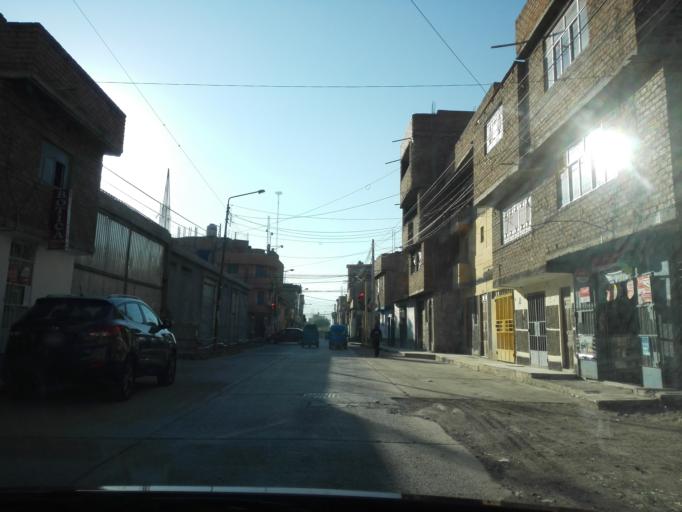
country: PE
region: Ayacucho
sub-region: Provincia de Huamanga
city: Ayacucho
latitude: -13.1566
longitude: -74.2223
